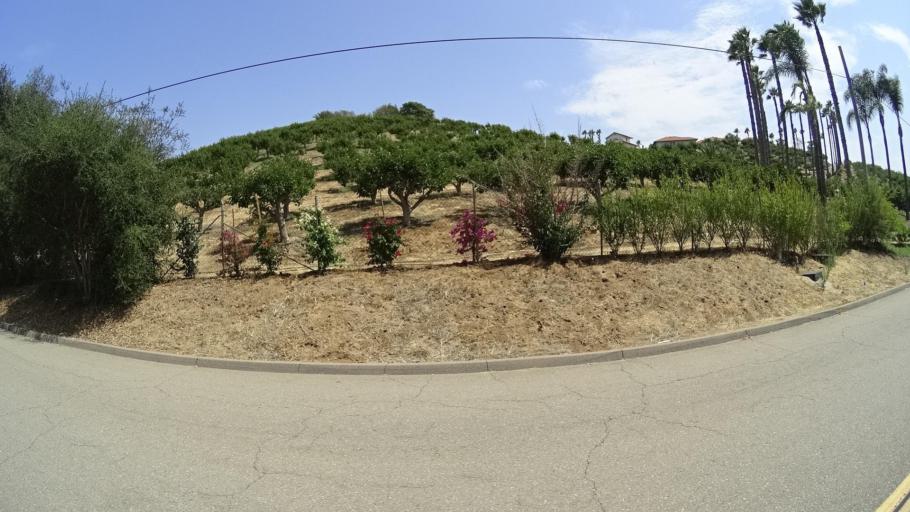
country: US
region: California
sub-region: San Diego County
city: Bonsall
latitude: 33.3060
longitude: -117.2160
